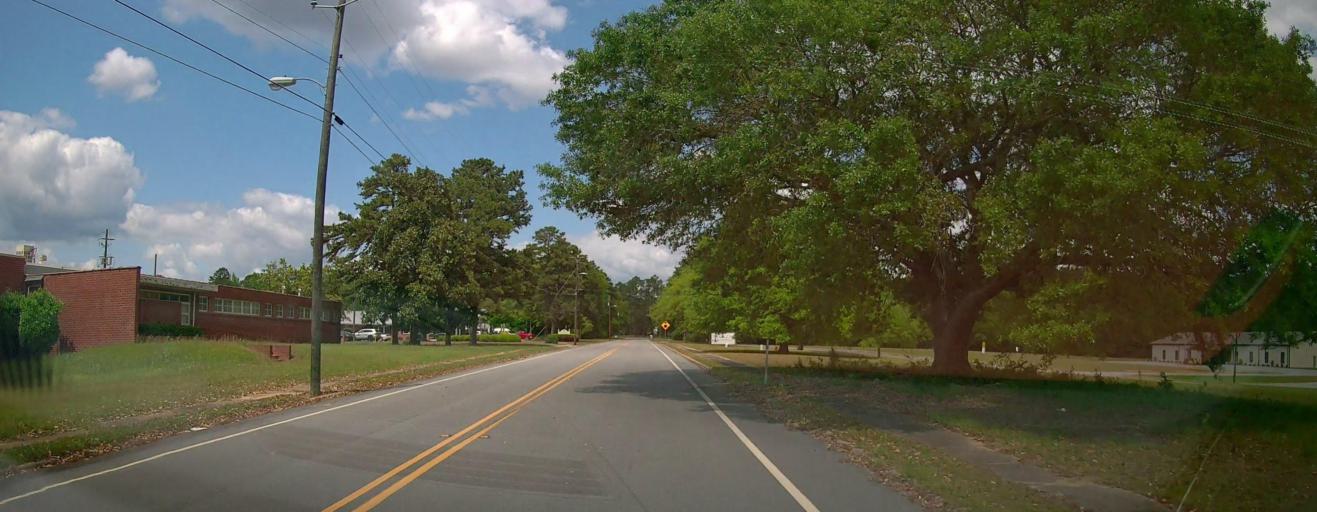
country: US
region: Georgia
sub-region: Treutlen County
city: Soperton
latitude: 32.3801
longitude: -82.5839
